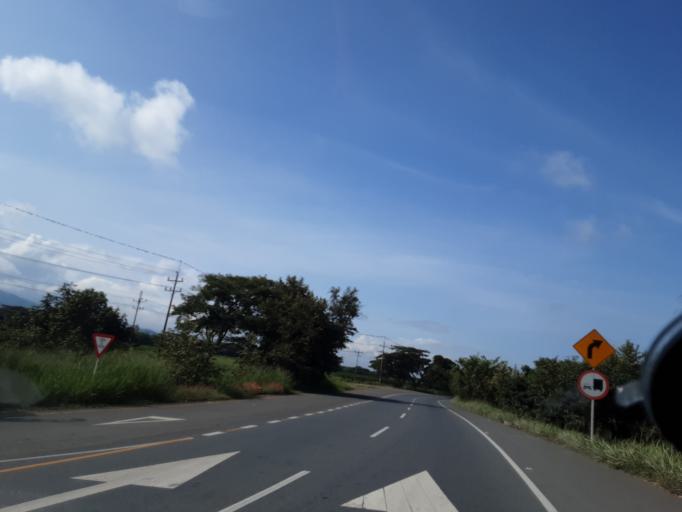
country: CO
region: Valle del Cauca
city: Buga
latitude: 3.8869
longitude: -76.3129
